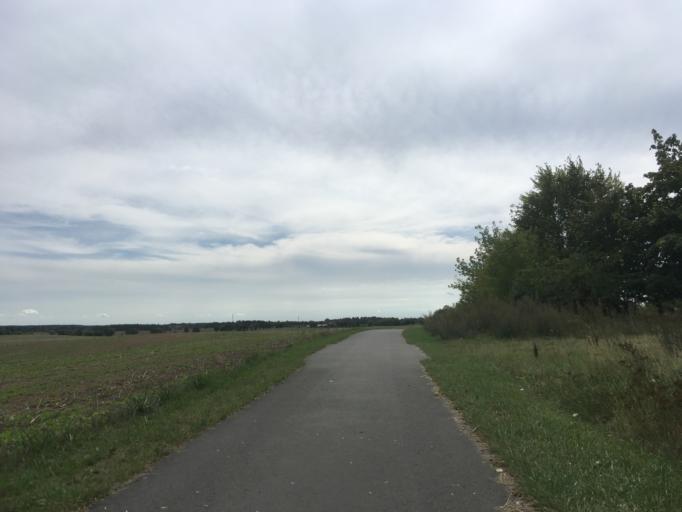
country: DE
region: Brandenburg
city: Mittenwalde
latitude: 53.2347
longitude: 13.6519
